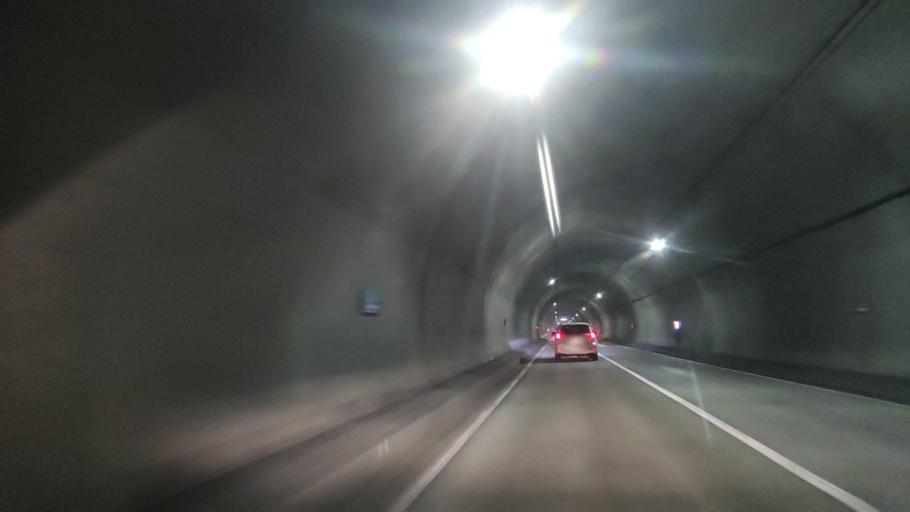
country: JP
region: Hokkaido
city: Ishikari
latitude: 43.5386
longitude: 141.3928
